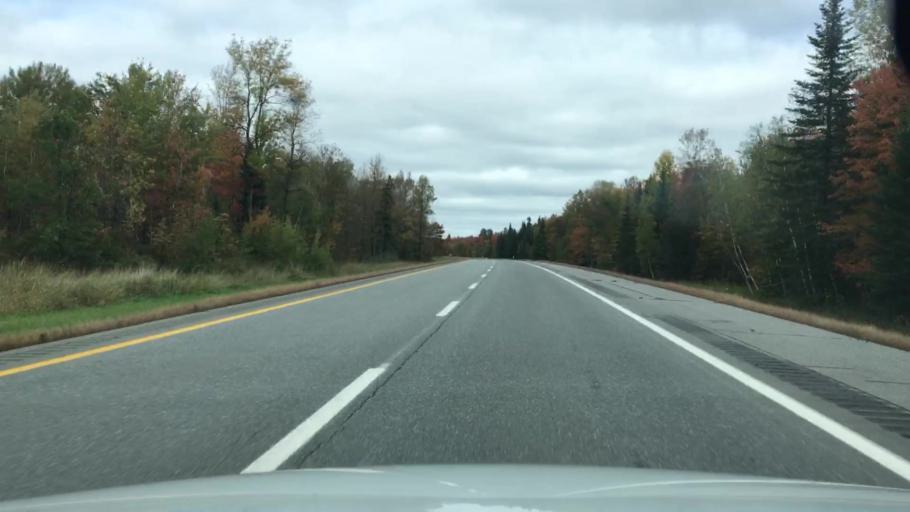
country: US
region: Maine
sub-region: Kennebec County
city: Clinton
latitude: 44.6643
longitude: -69.4937
